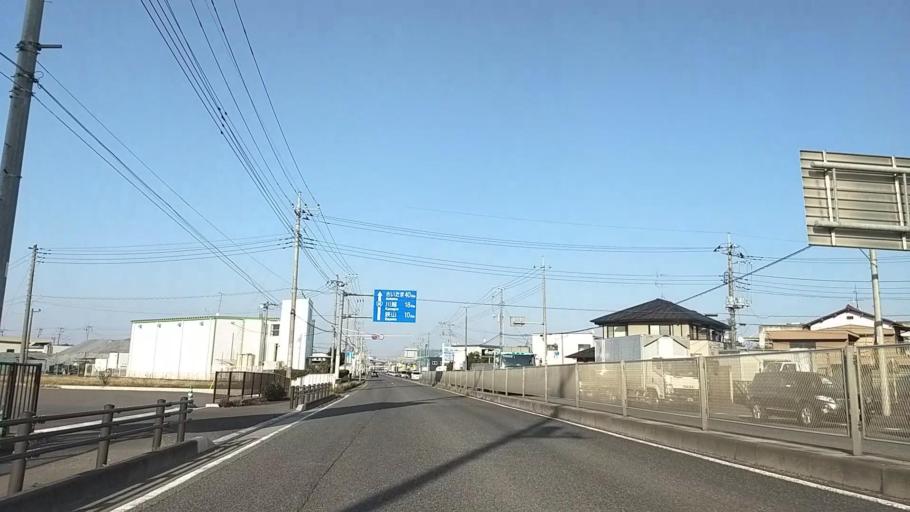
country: JP
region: Tokyo
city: Fussa
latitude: 35.7923
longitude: 139.3631
